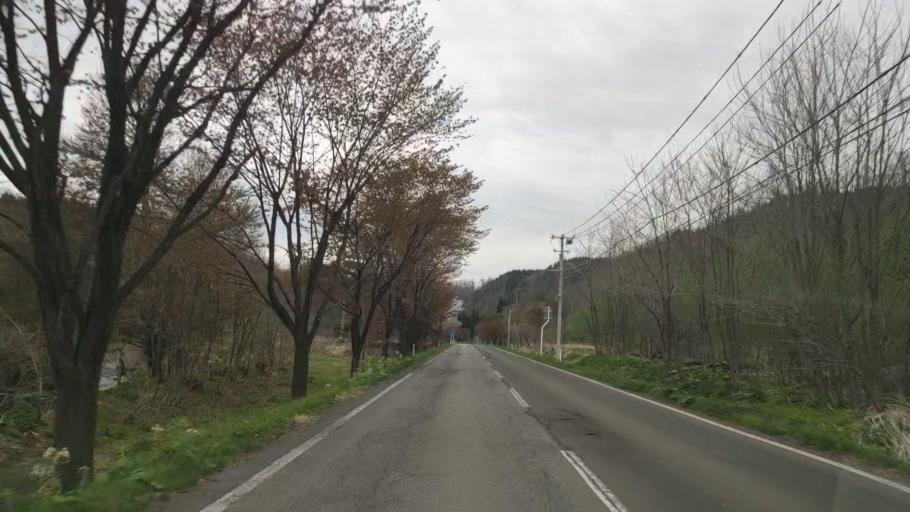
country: JP
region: Akita
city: Hanawa
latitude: 40.3550
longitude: 140.7804
